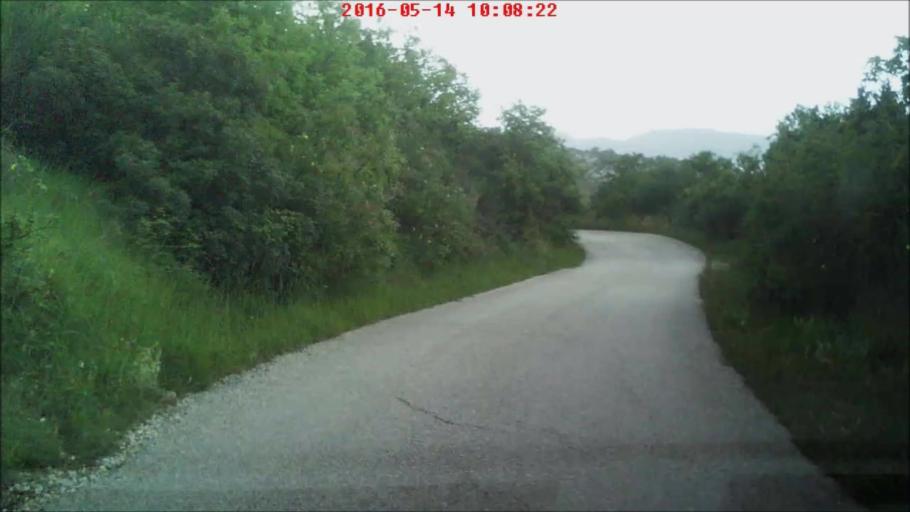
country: HR
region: Dubrovacko-Neretvanska
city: Podgora
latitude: 42.7489
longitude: 17.9352
